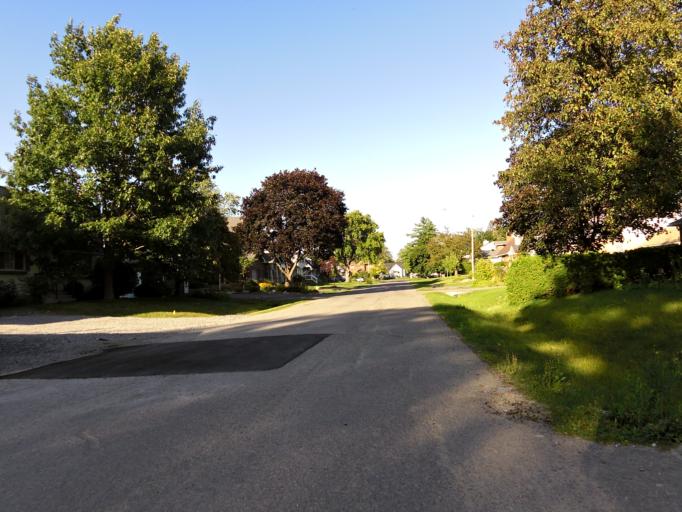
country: CA
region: Ontario
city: Ottawa
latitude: 45.3551
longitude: -75.7136
